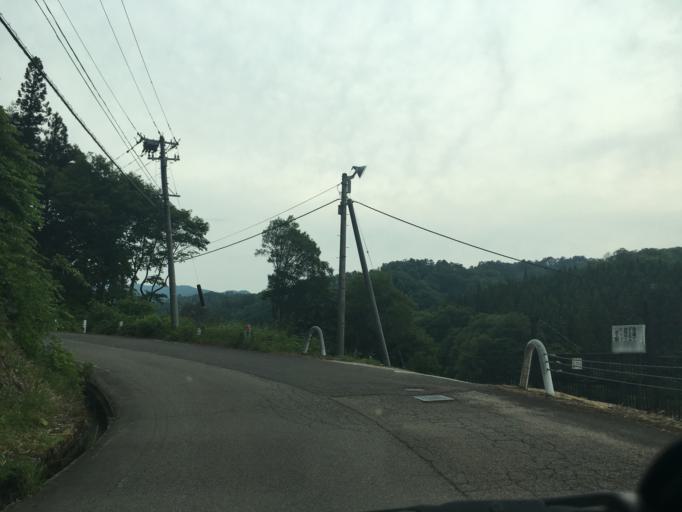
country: JP
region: Fukushima
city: Kitakata
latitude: 37.4876
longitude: 139.7786
